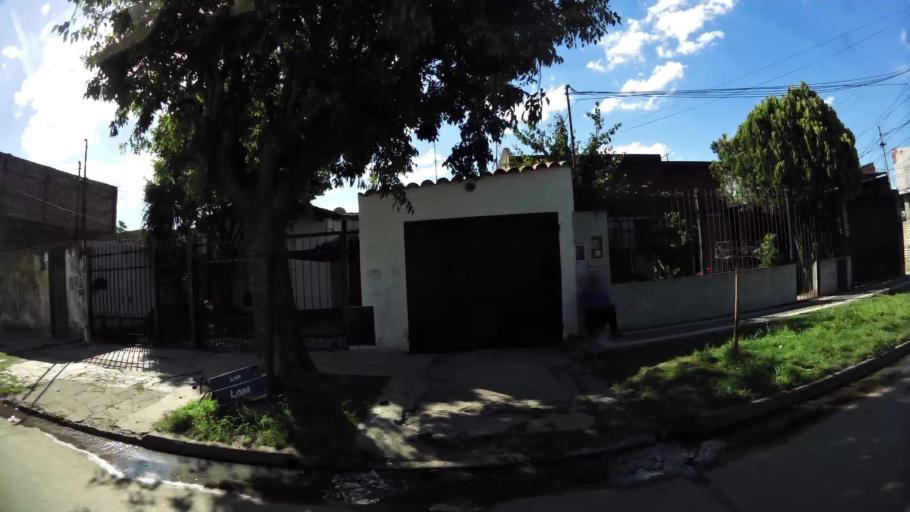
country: AR
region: Buenos Aires
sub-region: Partido de General San Martin
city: General San Martin
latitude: -34.5241
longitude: -58.5774
